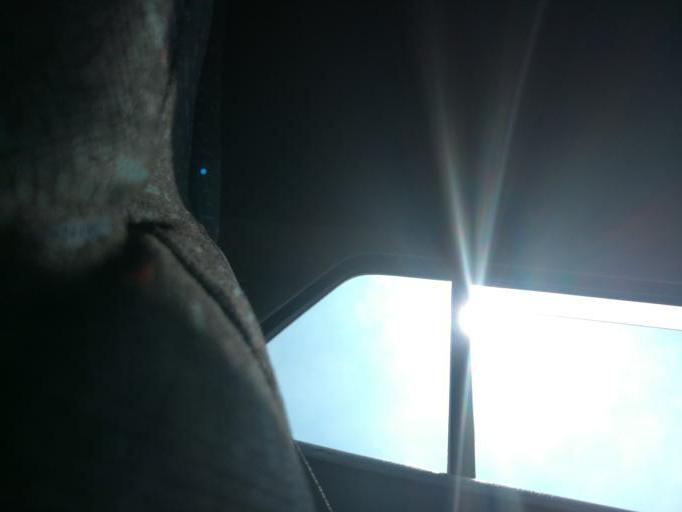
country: NG
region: Lagos
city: Lagos
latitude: 6.4552
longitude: 3.4011
